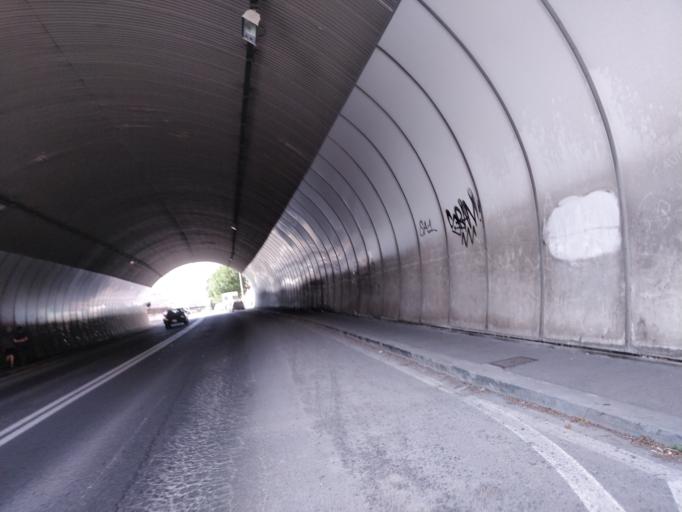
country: IT
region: Liguria
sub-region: Provincia di Savona
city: Savona
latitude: 44.3064
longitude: 8.4691
